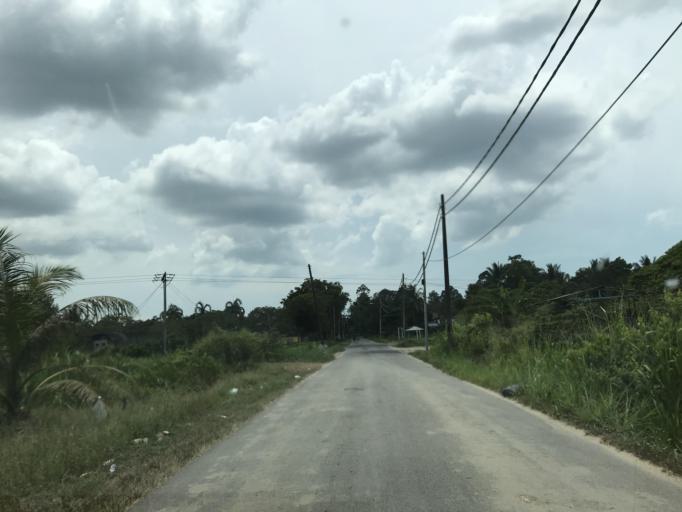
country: MY
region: Kelantan
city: Tumpat
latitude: 6.1486
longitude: 102.1877
